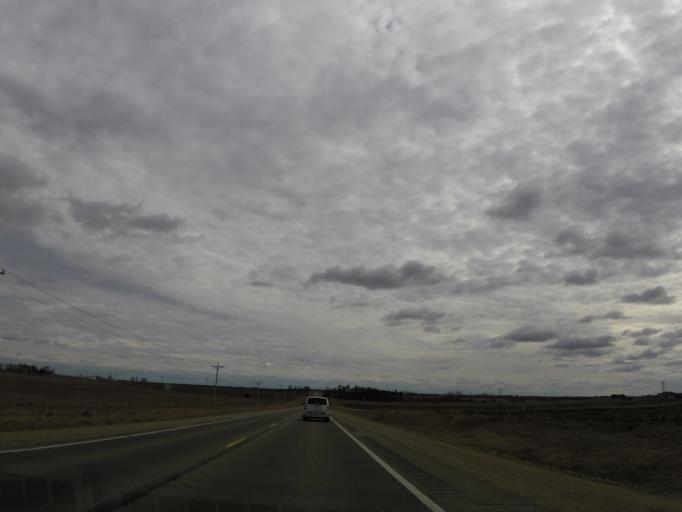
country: US
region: Iowa
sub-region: Chickasaw County
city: New Hampton
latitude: 43.1236
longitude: -92.2981
